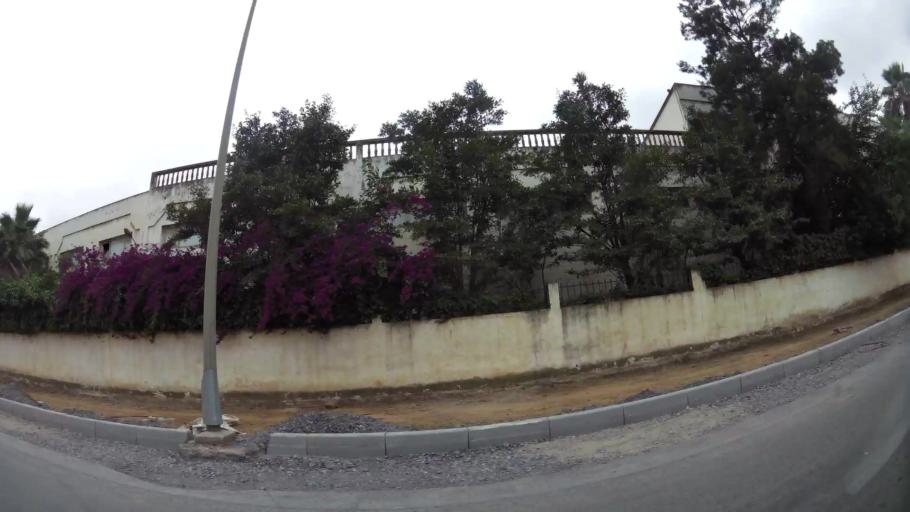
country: MA
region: Rabat-Sale-Zemmour-Zaer
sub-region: Rabat
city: Rabat
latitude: 33.9898
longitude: -6.8037
